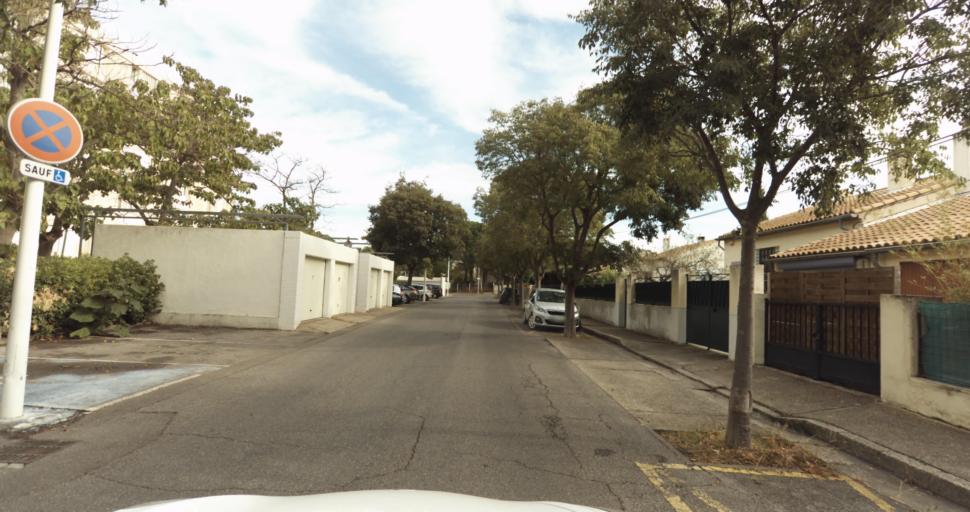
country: FR
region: Provence-Alpes-Cote d'Azur
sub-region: Departement des Bouches-du-Rhone
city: Miramas
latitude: 43.5904
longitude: 5.0078
